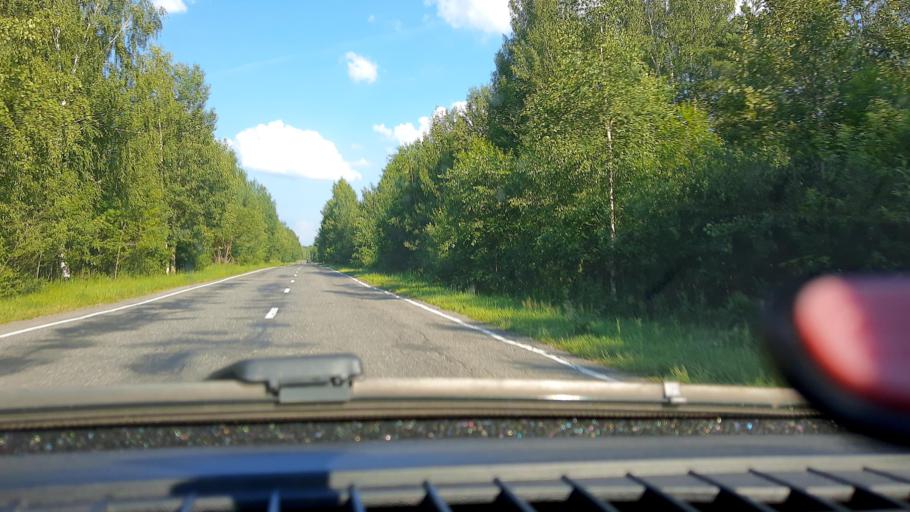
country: RU
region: Nizjnij Novgorod
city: Neklyudovo
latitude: 56.5121
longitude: 43.9480
